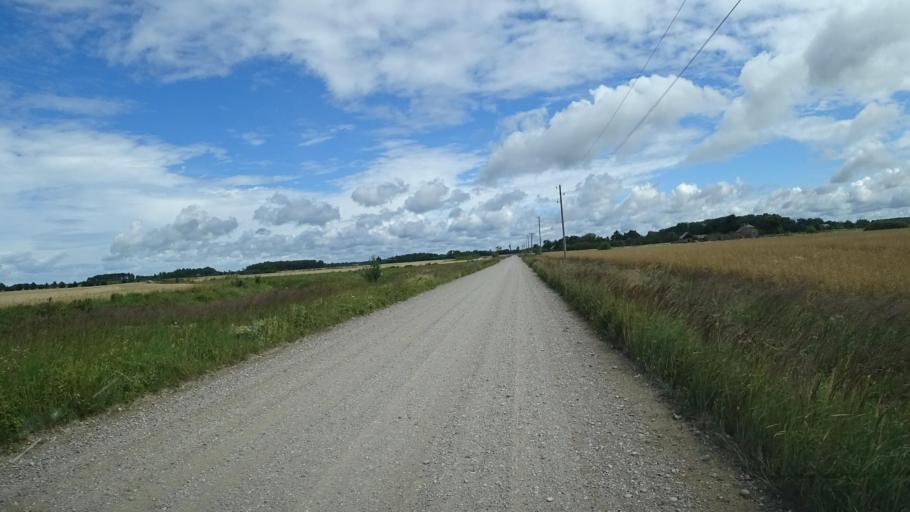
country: LV
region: Liepaja
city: Vec-Liepaja
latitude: 56.6520
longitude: 21.0512
